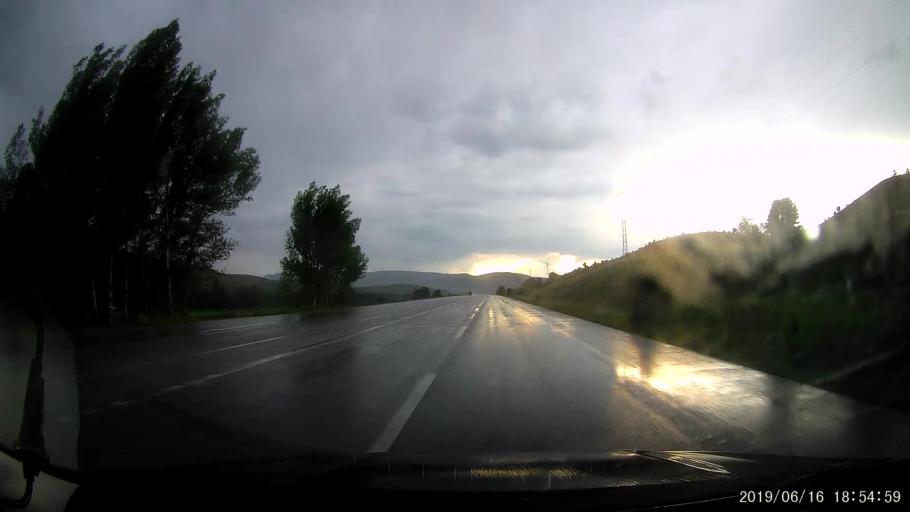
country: TR
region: Erzincan
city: Refahiye
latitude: 39.8985
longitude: 38.8397
